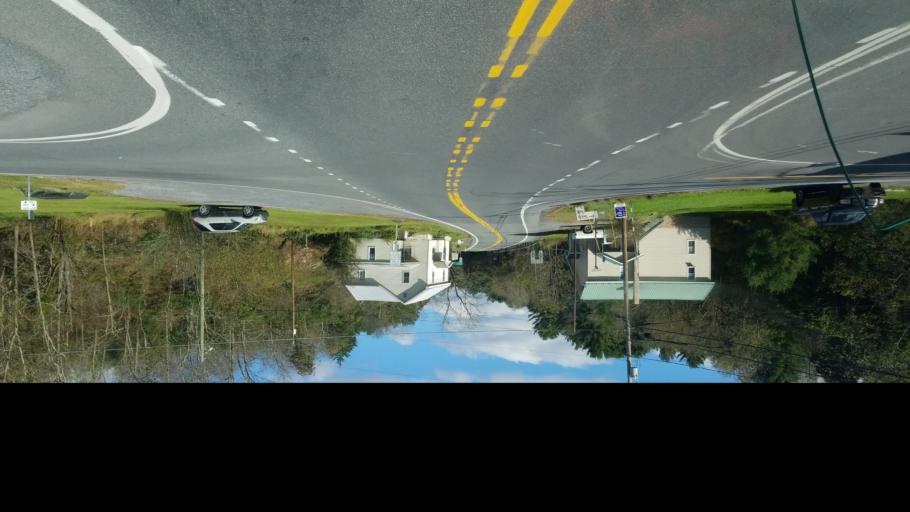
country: US
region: Pennsylvania
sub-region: Fulton County
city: McConnellsburg
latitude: 39.9877
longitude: -78.0600
